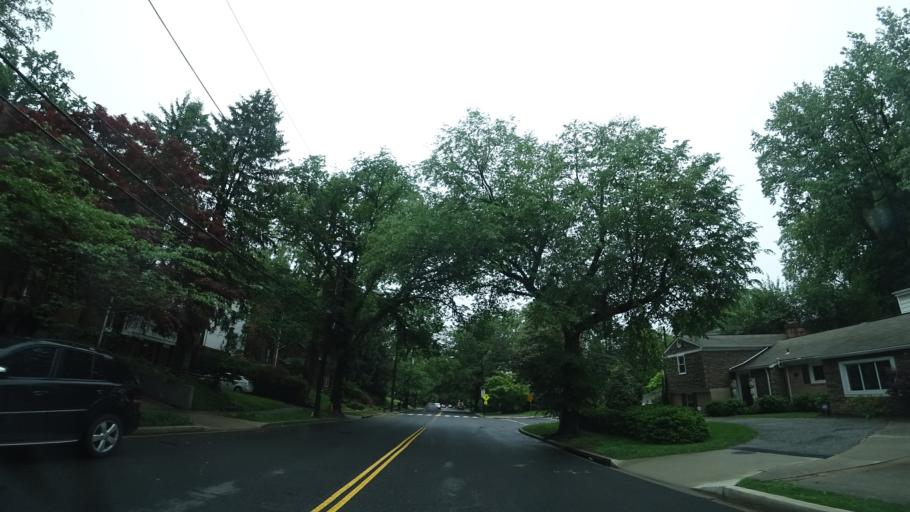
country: US
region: Maryland
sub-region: Montgomery County
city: Brookmont
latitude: 38.9298
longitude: -77.1002
